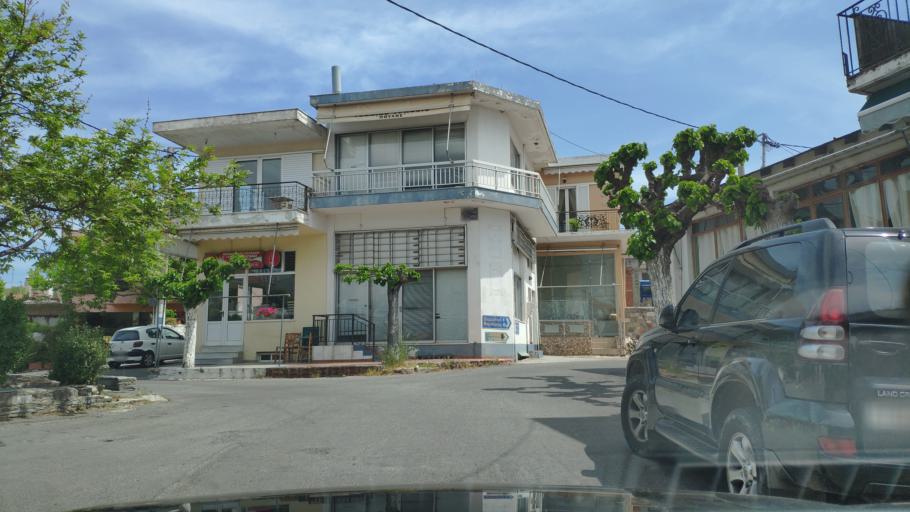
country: GR
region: Attica
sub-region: Nomarchia Anatolikis Attikis
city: Varnavas
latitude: 38.2236
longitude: 23.9236
